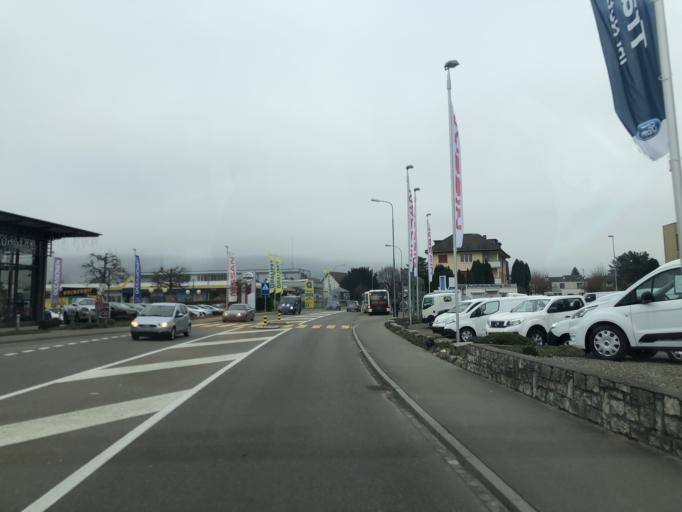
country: CH
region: Aargau
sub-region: Bezirk Baden
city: Turgi
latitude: 47.4892
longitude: 8.2459
